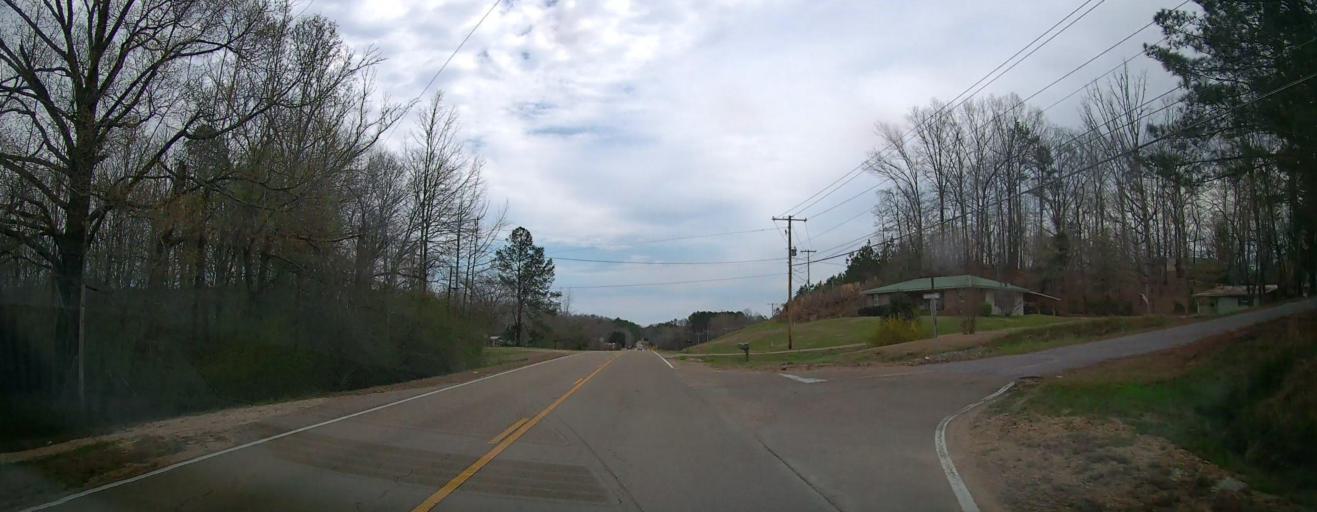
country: US
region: Mississippi
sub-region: Itawamba County
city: Fulton
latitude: 34.2546
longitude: -88.3106
